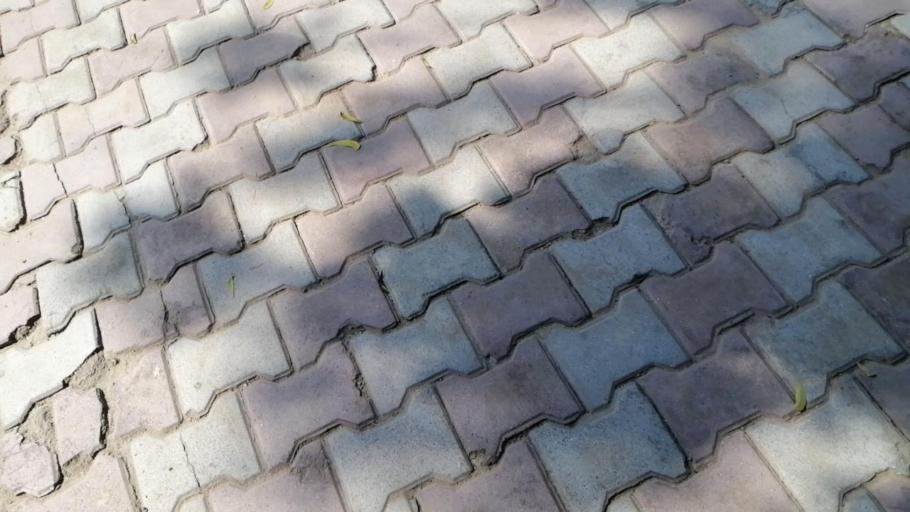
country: PK
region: Punjab
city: Kamalia
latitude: 30.7253
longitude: 72.6485
